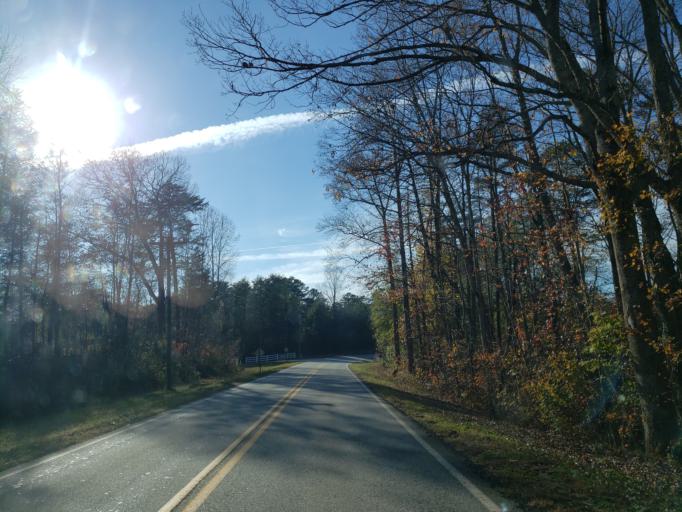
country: US
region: Georgia
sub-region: Lumpkin County
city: Dahlonega
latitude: 34.4653
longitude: -84.0167
